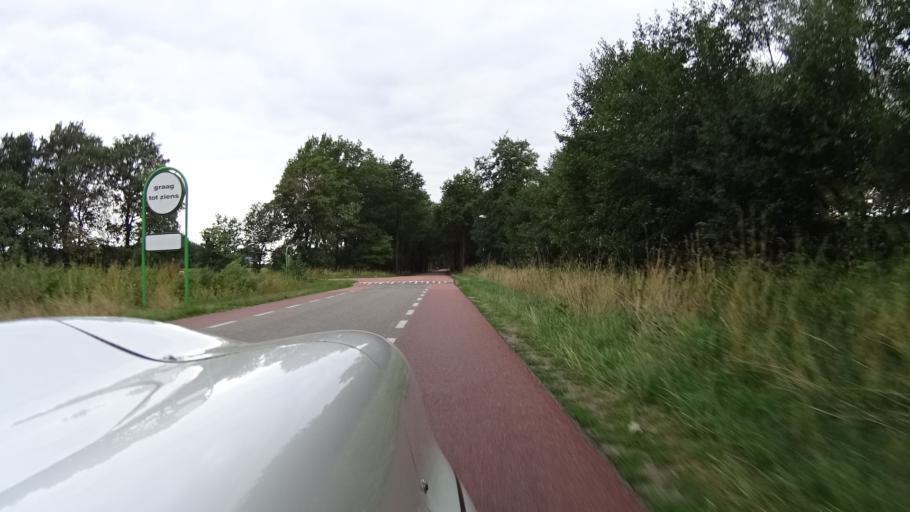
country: NL
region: North Brabant
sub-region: Gemeente Bernheze
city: Loosbroek
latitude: 51.6913
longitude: 5.4704
